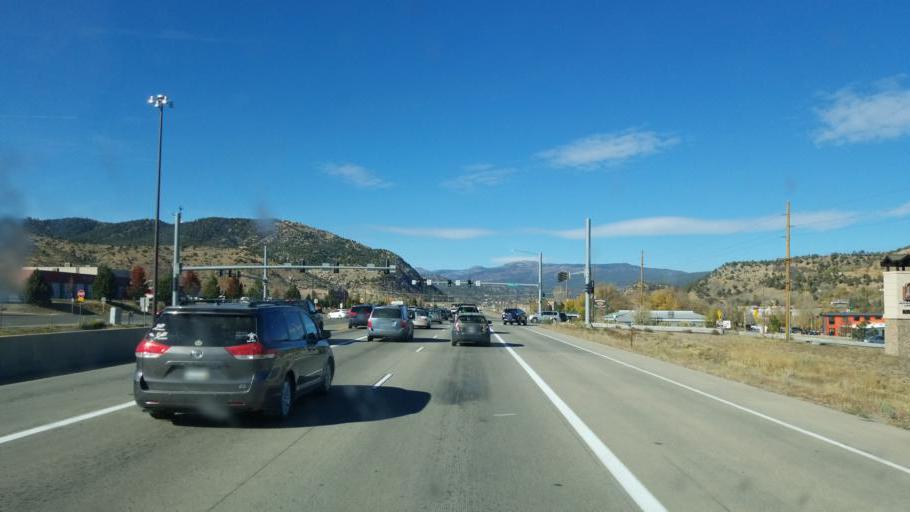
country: US
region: Colorado
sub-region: La Plata County
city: Durango
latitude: 37.2412
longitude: -107.8715
